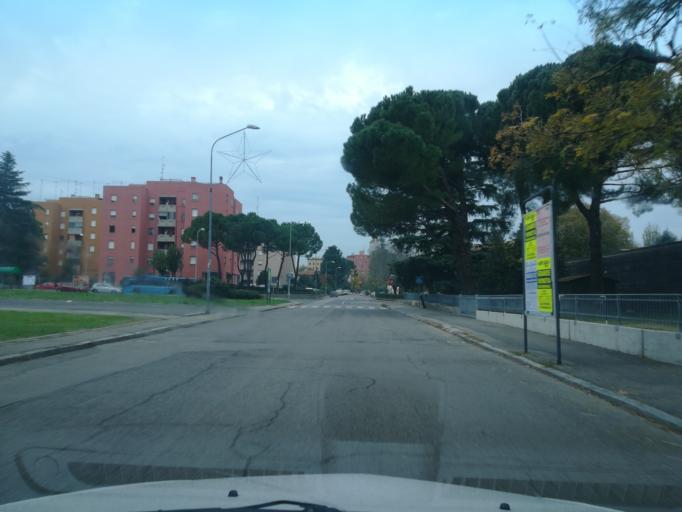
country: IT
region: Emilia-Romagna
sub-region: Provincia di Bologna
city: Imola
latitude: 44.3650
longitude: 11.6901
